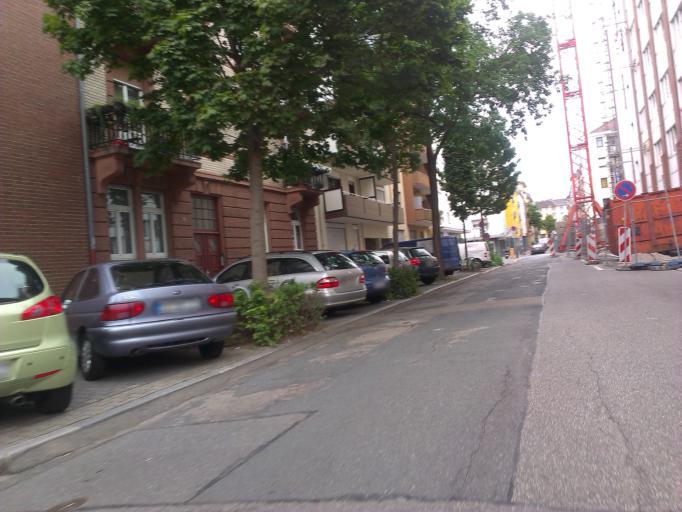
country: DE
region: Baden-Wuerttemberg
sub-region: Karlsruhe Region
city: Mannheim
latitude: 49.4795
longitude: 8.4749
